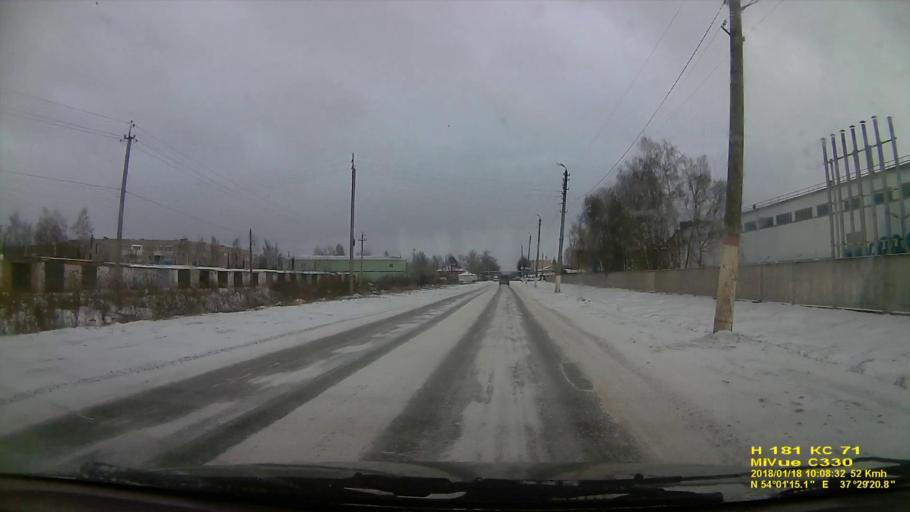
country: RU
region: Tula
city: Pervomayskiy
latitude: 54.0207
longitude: 37.4892
